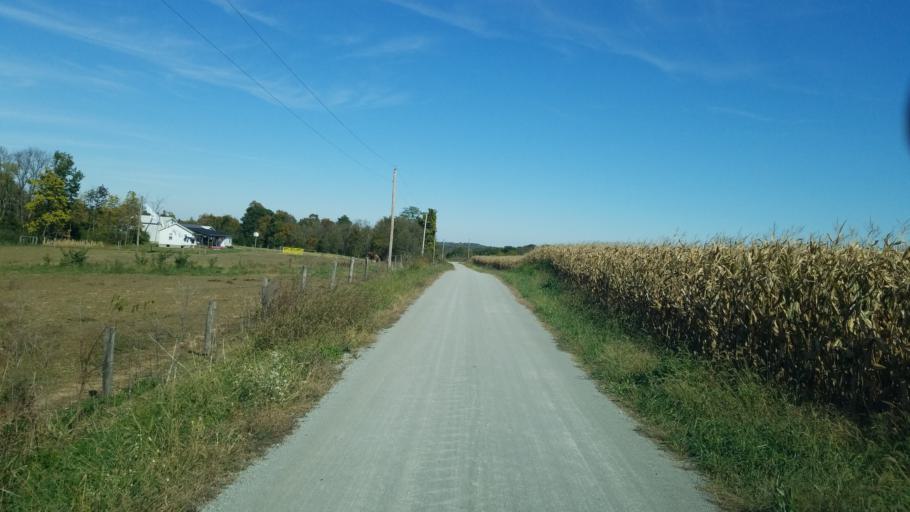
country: US
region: Ohio
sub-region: Highland County
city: Leesburg
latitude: 39.2939
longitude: -83.4828
